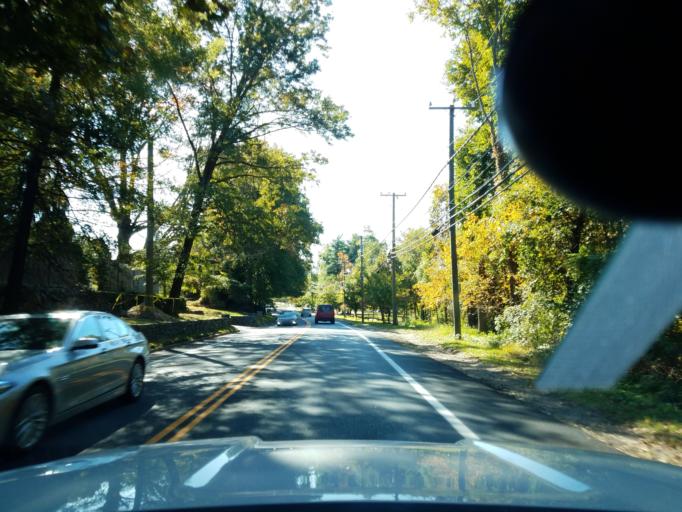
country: US
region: Connecticut
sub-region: Fairfield County
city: Cos Cob
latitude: 41.0605
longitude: -73.6184
